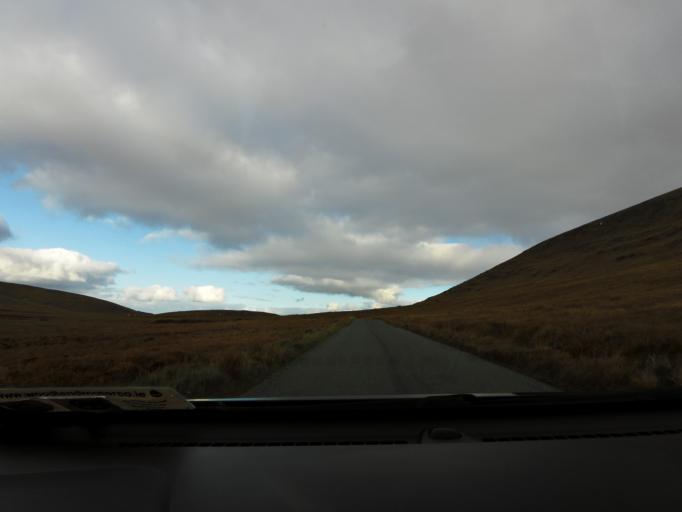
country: IE
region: Connaught
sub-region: Maigh Eo
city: Belmullet
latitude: 53.9328
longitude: -10.0008
